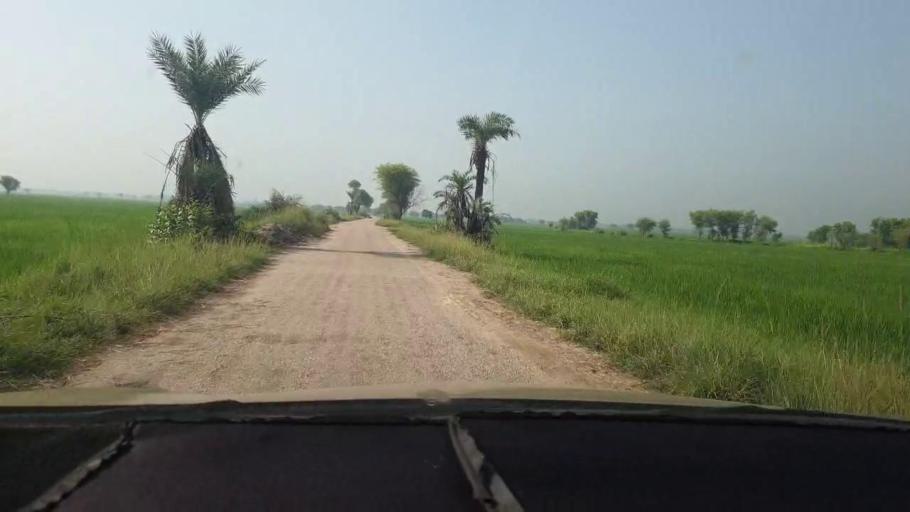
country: PK
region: Sindh
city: Kambar
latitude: 27.6313
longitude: 68.0898
